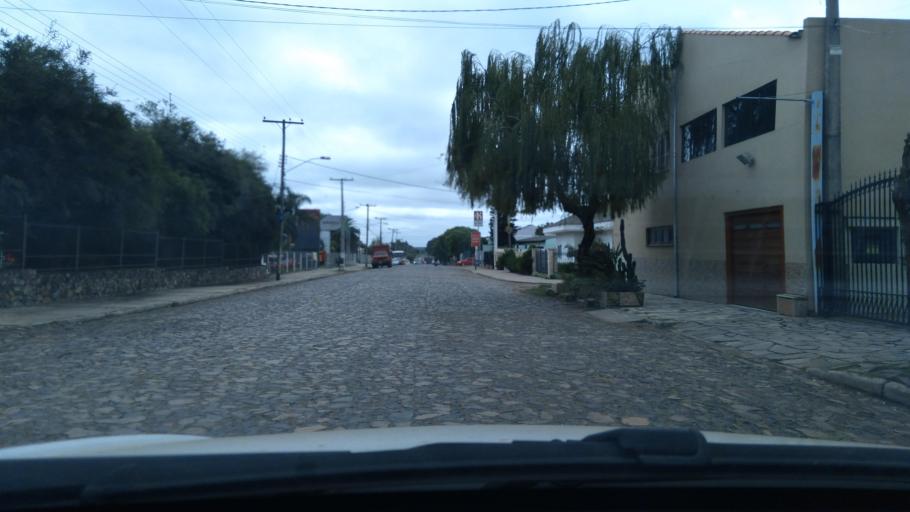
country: BR
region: Rio Grande do Sul
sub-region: Dom Pedrito
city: Dom Pedrito
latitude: -30.9659
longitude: -54.6729
